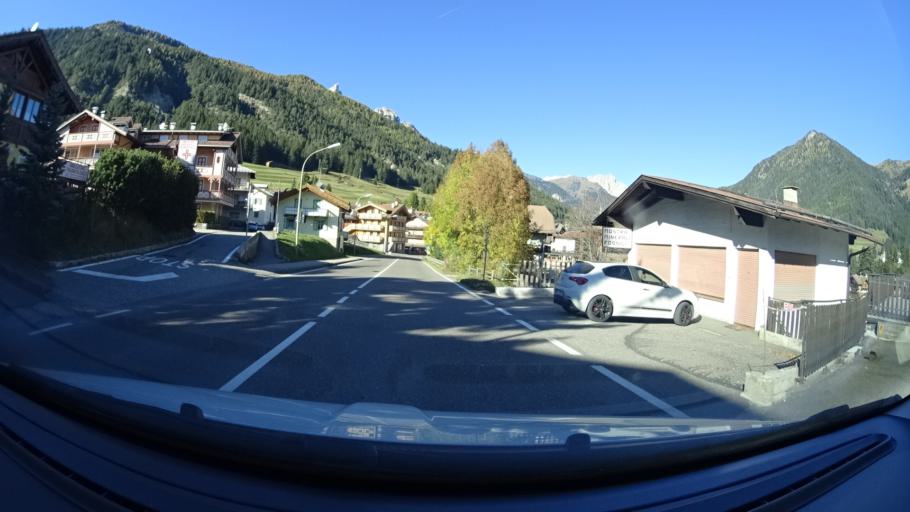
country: IT
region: Trentino-Alto Adige
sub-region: Provincia di Trento
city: Pozza di Fassa
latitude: 46.4257
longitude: 11.6828
